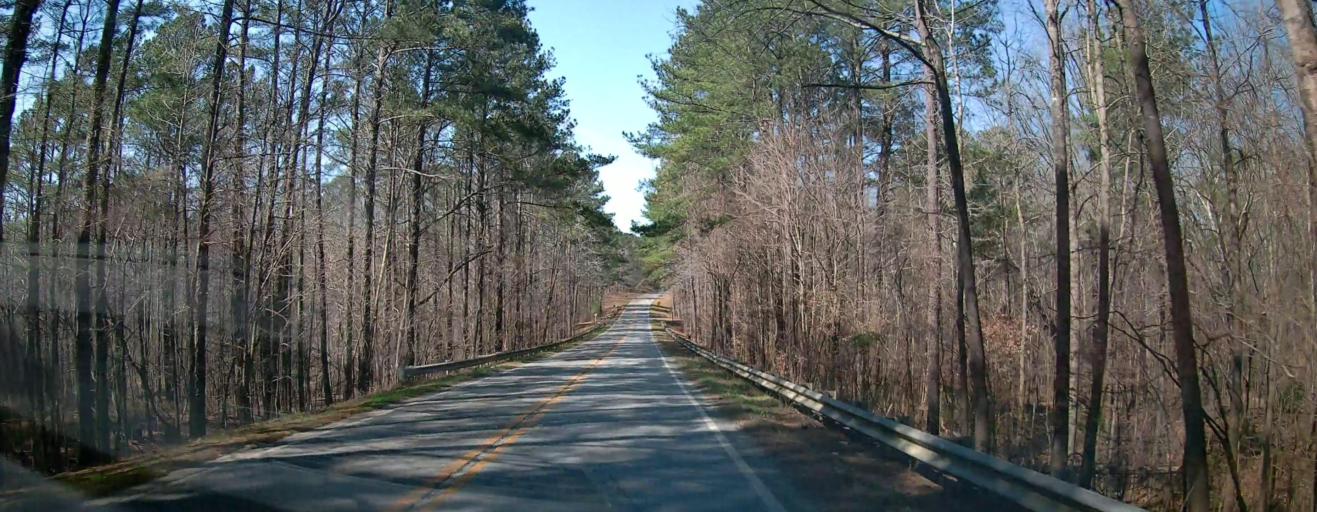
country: US
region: Georgia
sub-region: Jones County
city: Gray
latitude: 32.9260
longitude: -83.5324
